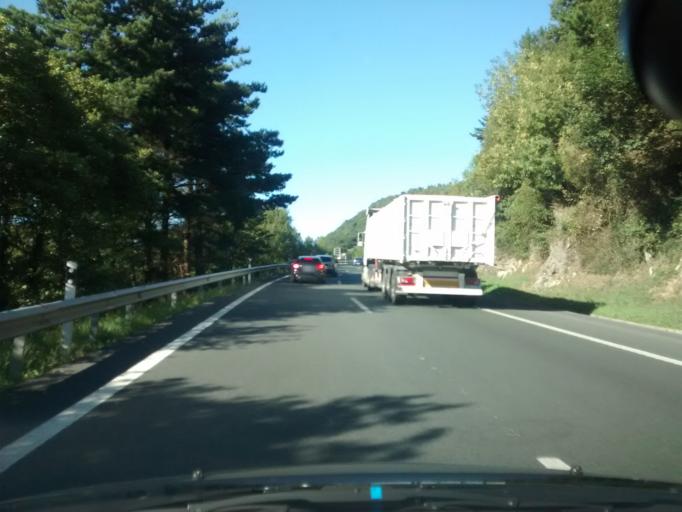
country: ES
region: Basque Country
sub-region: Provincia de Guipuzcoa
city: Mendaro
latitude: 43.2721
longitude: -2.3680
